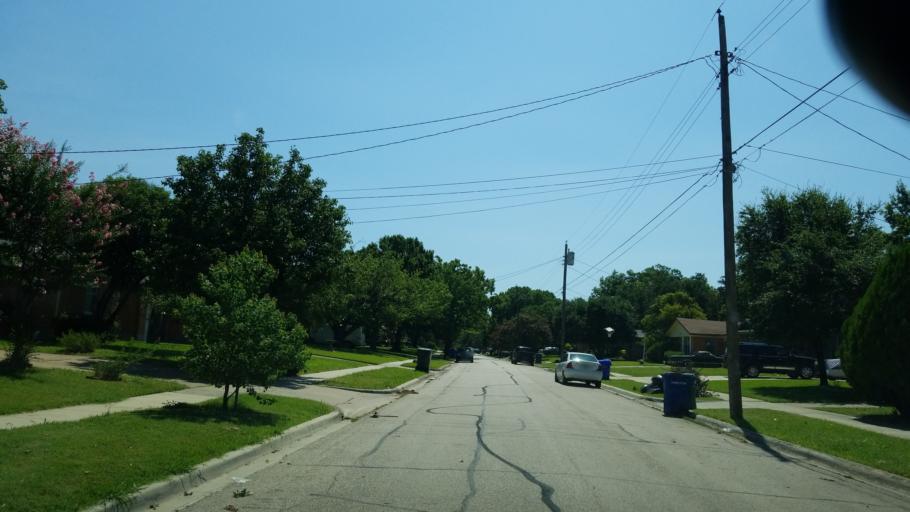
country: US
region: Texas
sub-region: Dallas County
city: Carrollton
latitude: 32.9667
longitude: -96.9046
